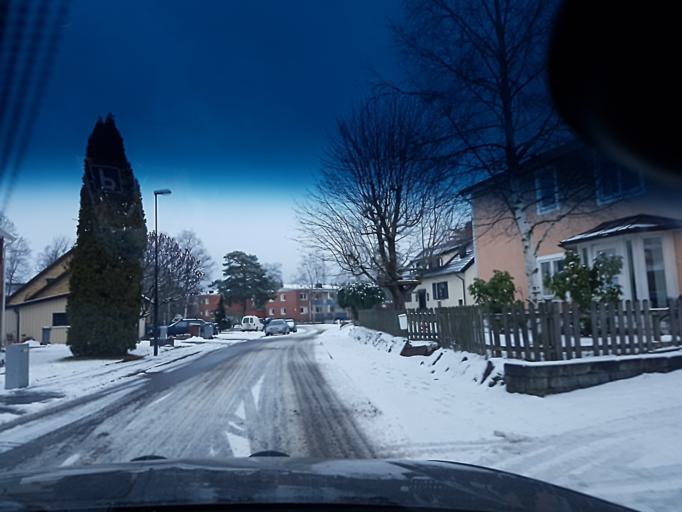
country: SE
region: Joenkoeping
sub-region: Vetlanda Kommun
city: Vetlanda
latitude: 57.4223
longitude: 15.0955
